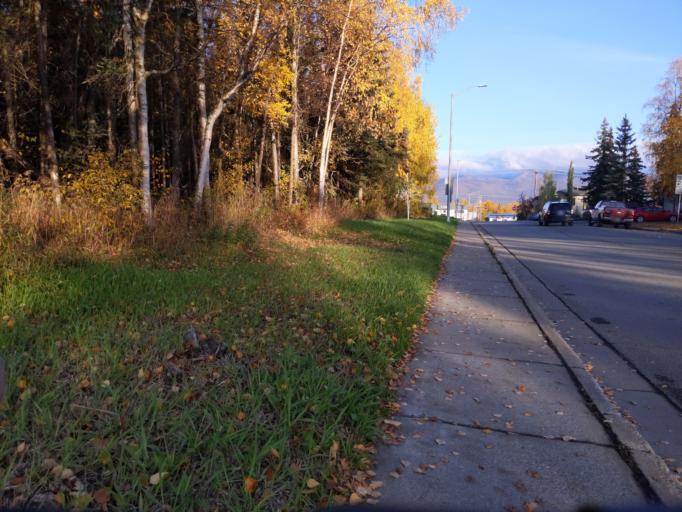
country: US
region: Alaska
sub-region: Anchorage Municipality
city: Anchorage
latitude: 61.1556
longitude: -149.8677
